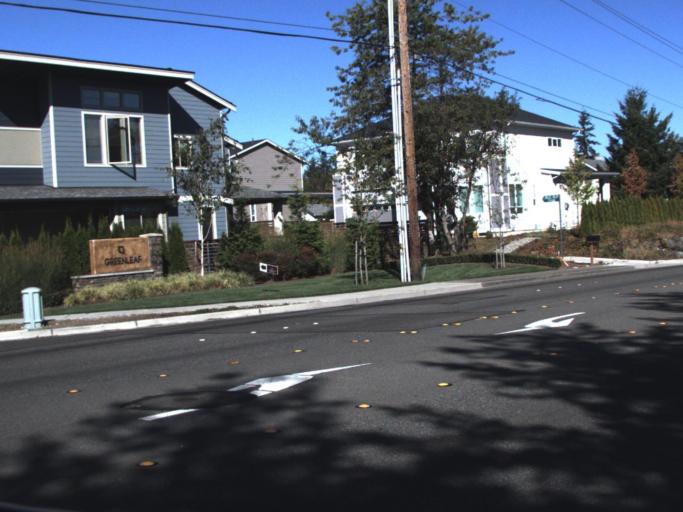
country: US
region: Washington
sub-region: King County
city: East Hill-Meridian
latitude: 47.4347
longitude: -122.1970
